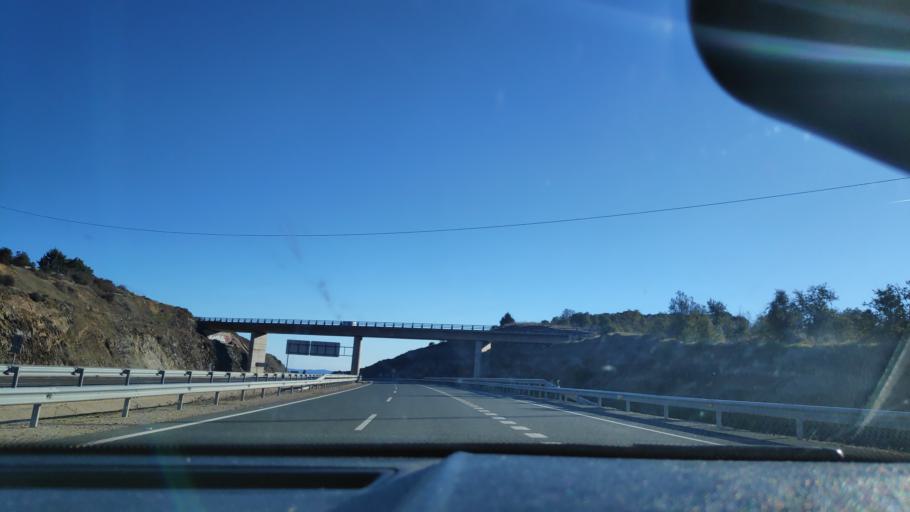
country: ES
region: Extremadura
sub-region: Provincia de Badajoz
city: Monesterio
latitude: 38.0814
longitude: -6.2597
